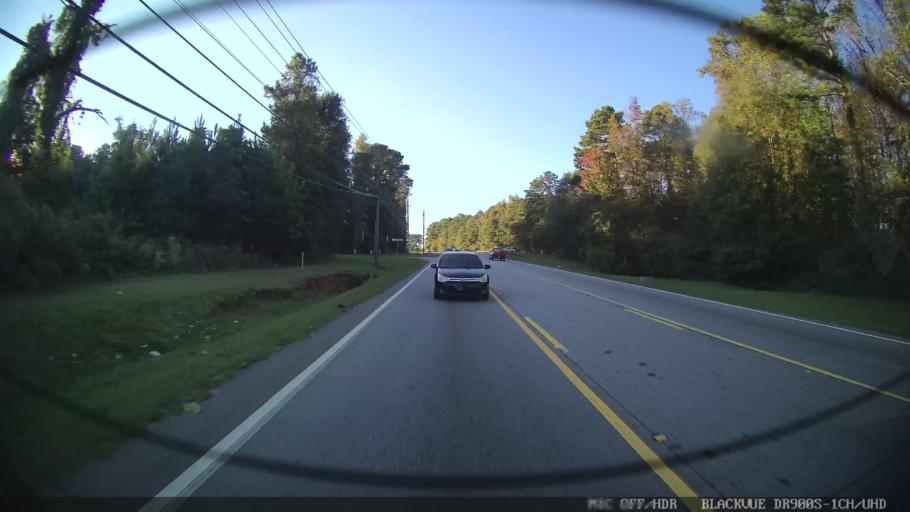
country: US
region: Georgia
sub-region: Henry County
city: Stockbridge
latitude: 33.5765
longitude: -84.2696
